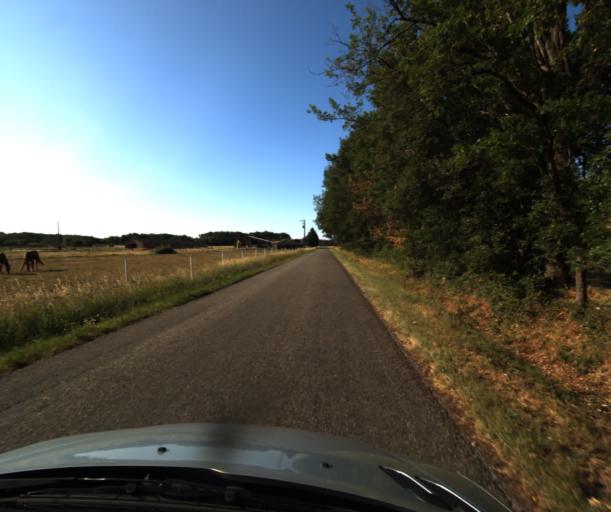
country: FR
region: Midi-Pyrenees
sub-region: Departement du Tarn-et-Garonne
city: Saint-Porquier
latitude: 44.0615
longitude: 1.2082
